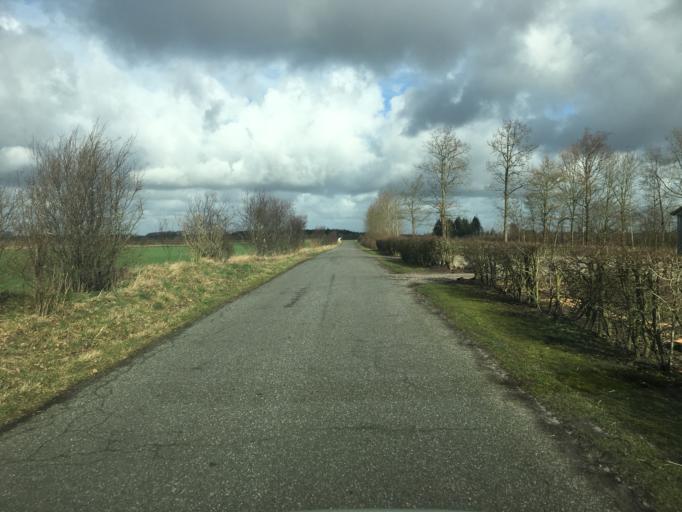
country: DK
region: South Denmark
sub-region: Aabenraa Kommune
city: Krusa
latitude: 54.9164
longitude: 9.3579
